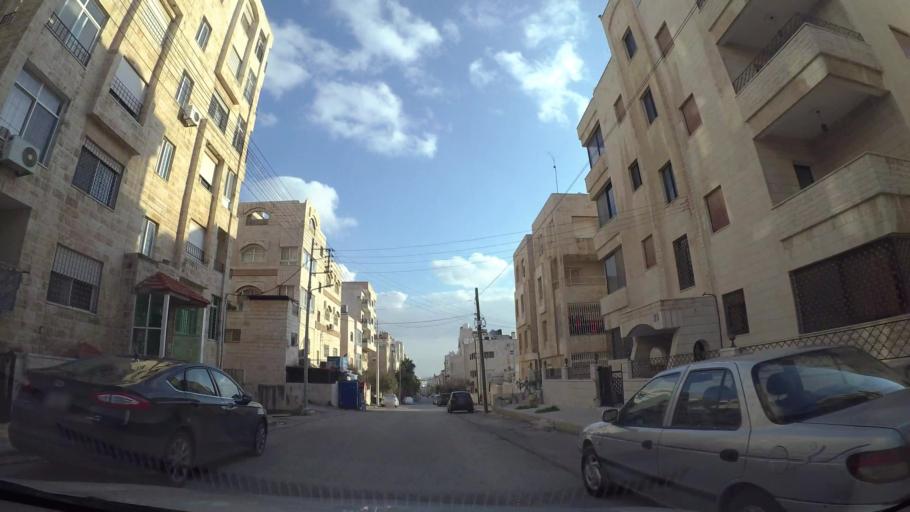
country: JO
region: Amman
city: Al Jubayhah
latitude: 31.9966
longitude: 35.8671
